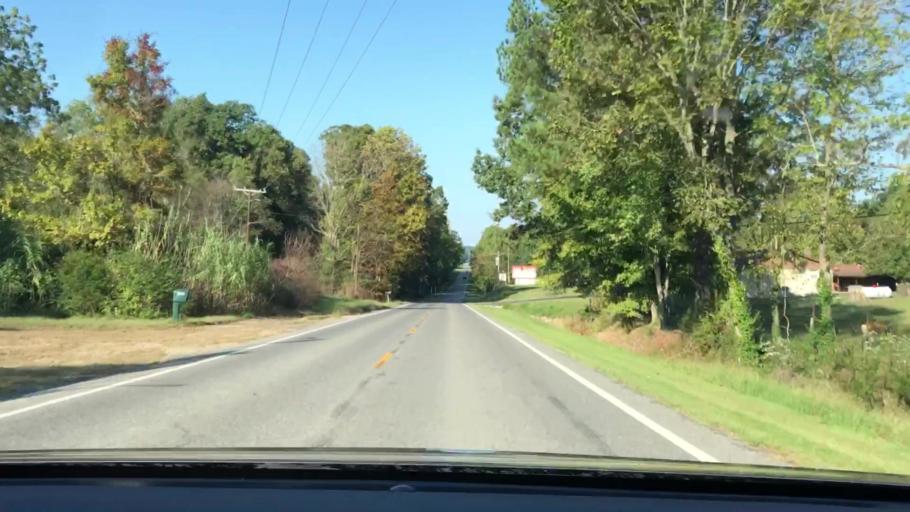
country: US
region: Kentucky
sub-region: Marshall County
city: Benton
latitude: 36.7645
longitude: -88.2186
